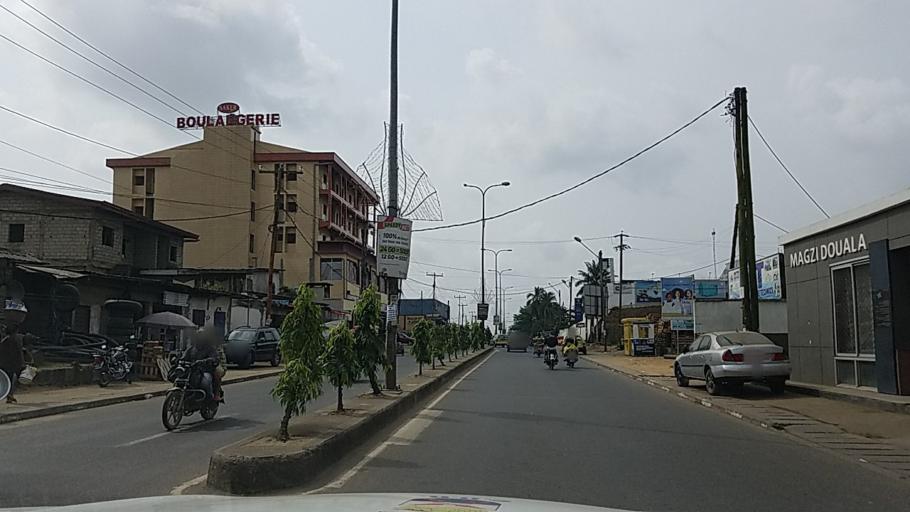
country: CM
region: Littoral
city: Douala
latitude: 4.0388
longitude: 9.7416
